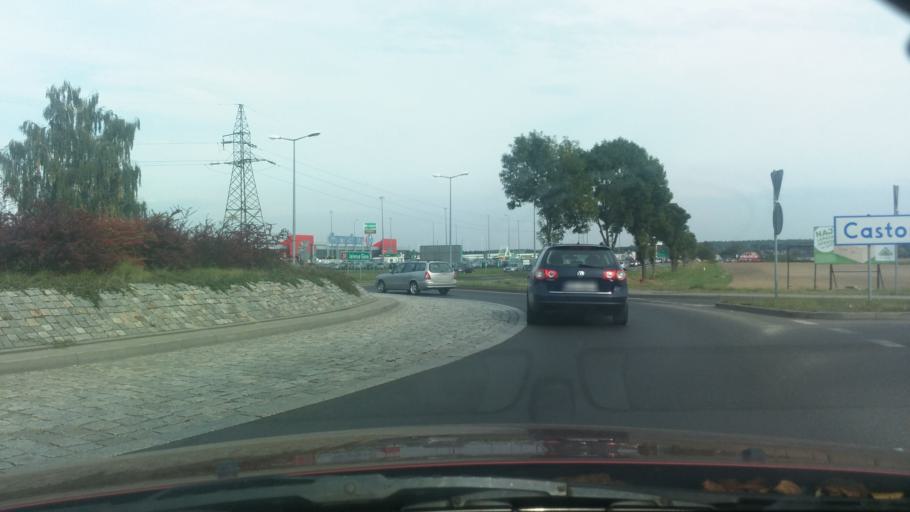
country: PL
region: Lower Silesian Voivodeship
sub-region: Powiat zgorzelecki
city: Lagow
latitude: 51.1536
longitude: 15.0289
